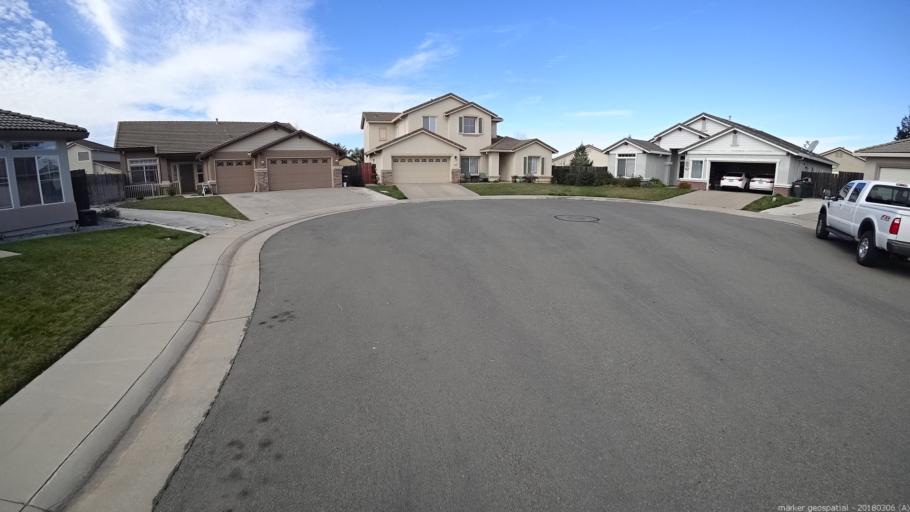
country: US
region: California
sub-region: Sacramento County
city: Vineyard
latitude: 38.4707
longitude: -121.3213
